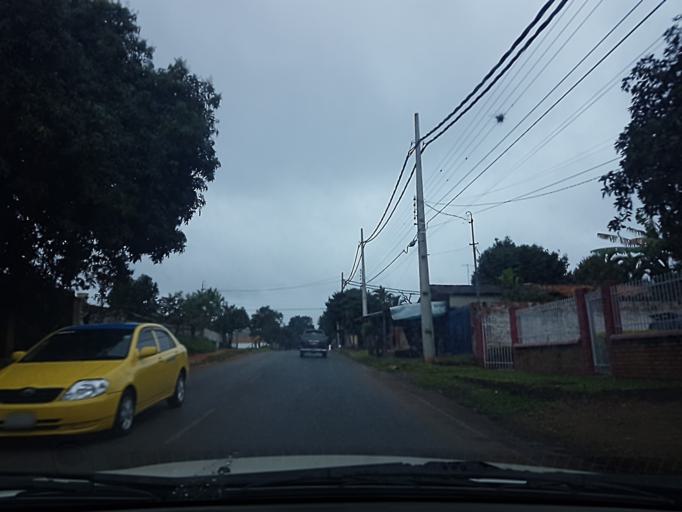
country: PY
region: Central
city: San Lorenzo
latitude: -25.2729
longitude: -57.4718
